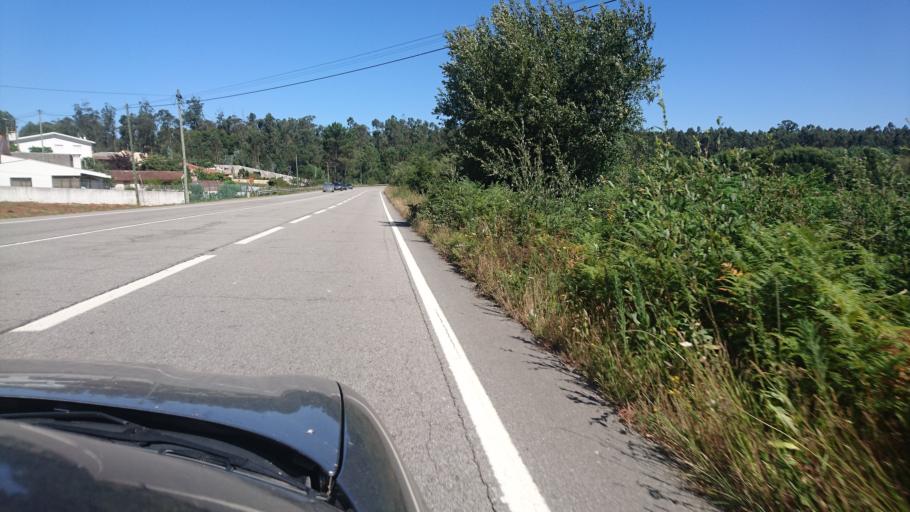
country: PT
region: Aveiro
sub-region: Santa Maria da Feira
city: Rio Meao
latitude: 40.9276
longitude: -8.5831
